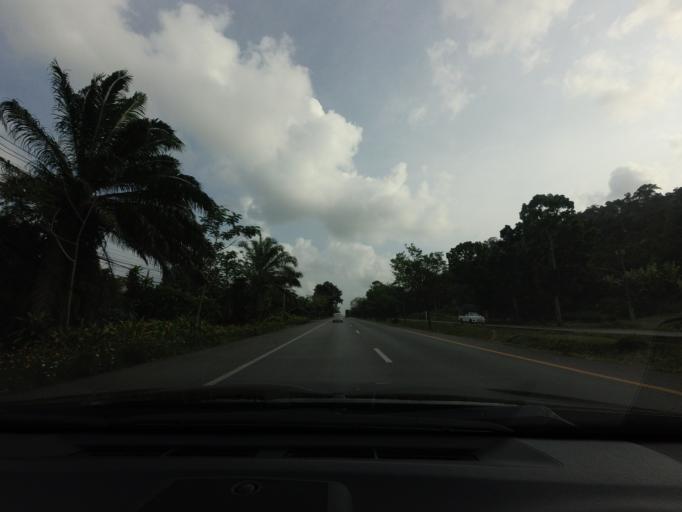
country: TH
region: Chumphon
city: Thung Tako
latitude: 10.1045
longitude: 99.0799
